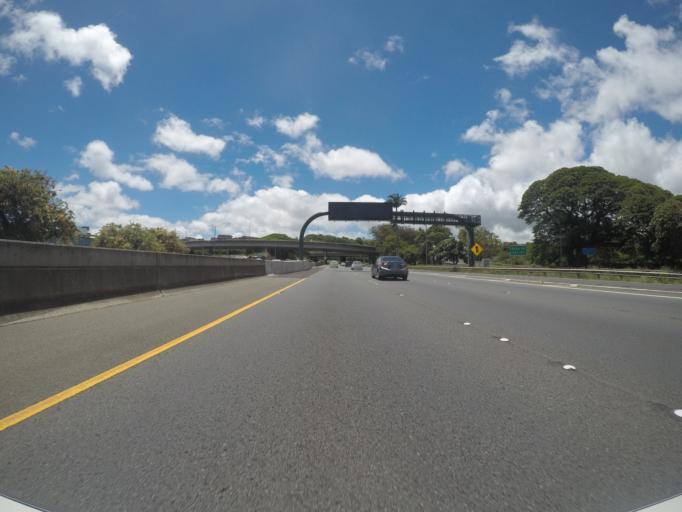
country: US
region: Hawaii
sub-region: Honolulu County
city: Halawa Heights
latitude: 21.3473
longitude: -157.8947
